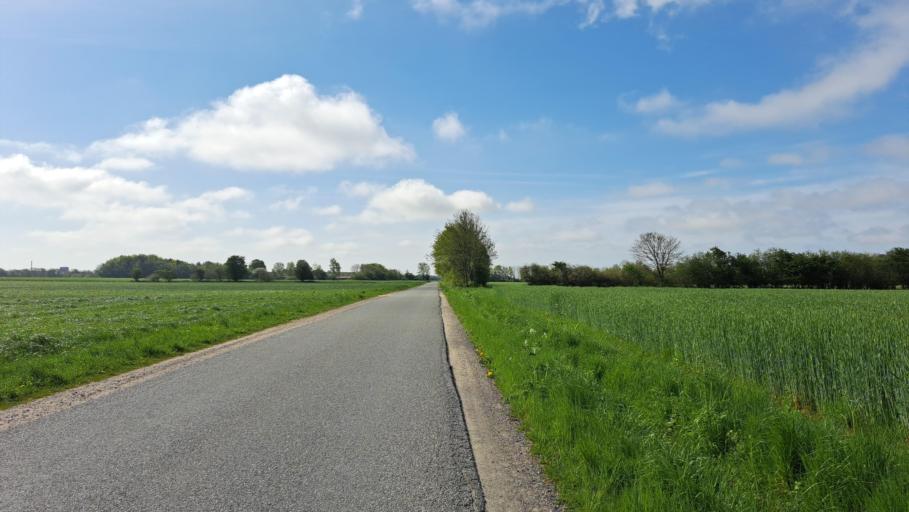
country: DK
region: Central Jutland
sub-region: Hedensted Kommune
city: Hedensted
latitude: 55.8049
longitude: 9.6550
